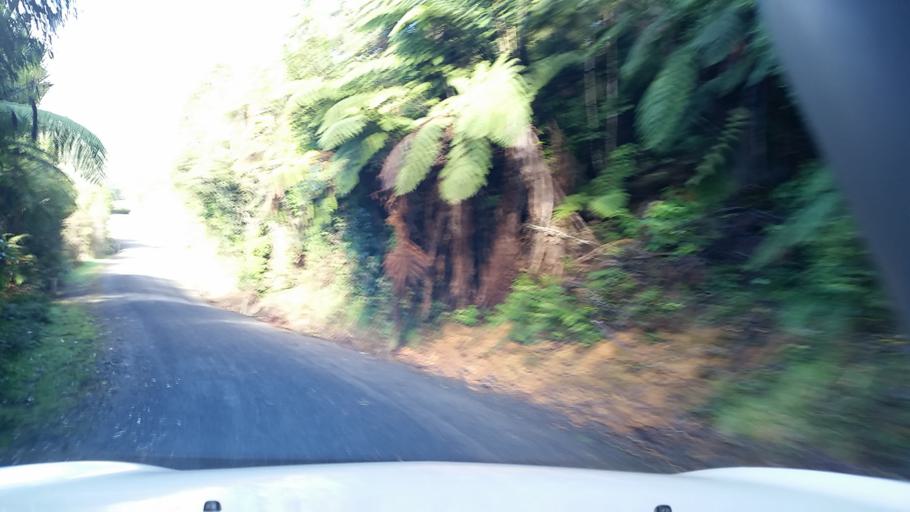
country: NZ
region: Waikato
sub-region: Matamata-Piako District
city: Matamata
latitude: -37.8166
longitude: 175.6316
